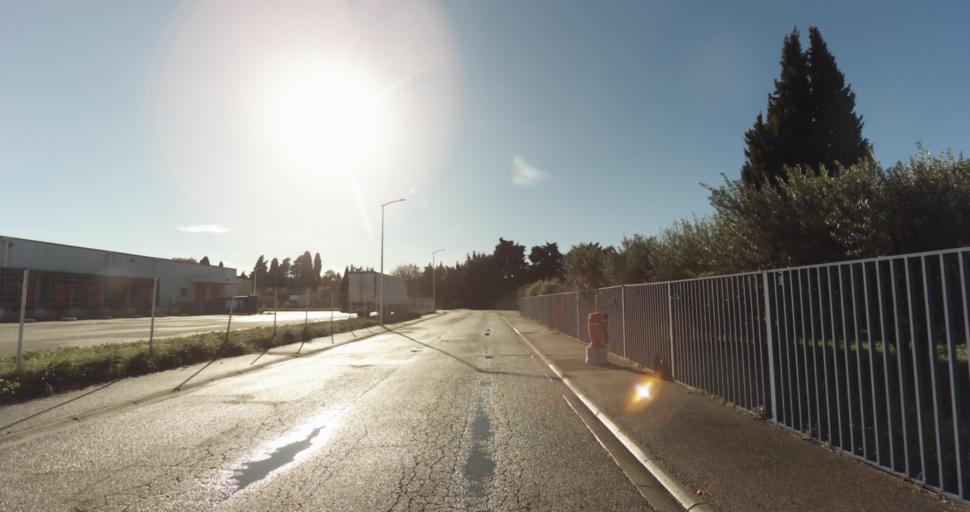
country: FR
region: Provence-Alpes-Cote d'Azur
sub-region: Departement des Bouches-du-Rhone
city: Rognonas
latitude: 43.8973
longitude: 4.8156
